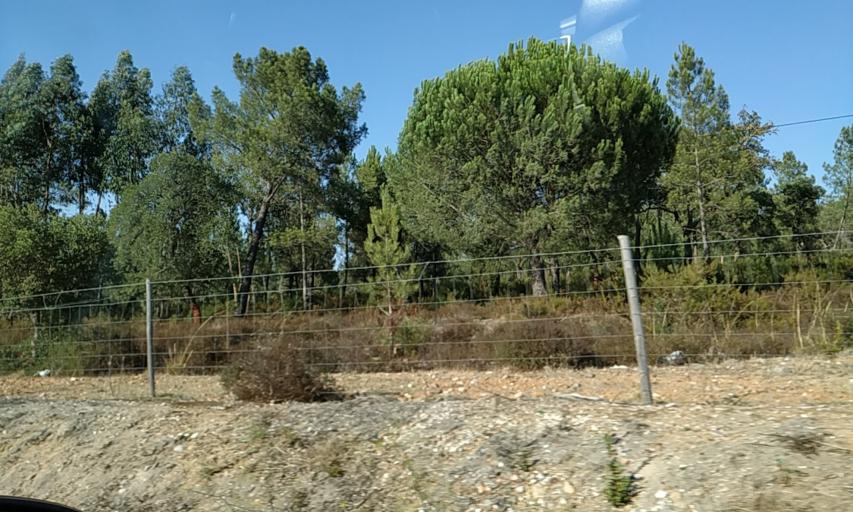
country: PT
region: Santarem
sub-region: Almeirim
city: Fazendas de Almeirim
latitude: 39.1202
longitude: -8.5991
